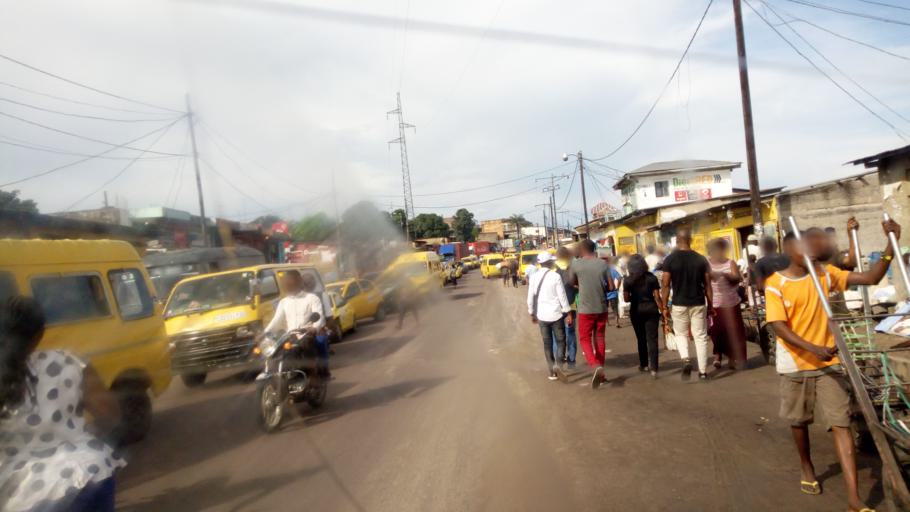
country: CD
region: Kinshasa
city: Kinshasa
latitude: -4.4468
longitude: 15.2502
